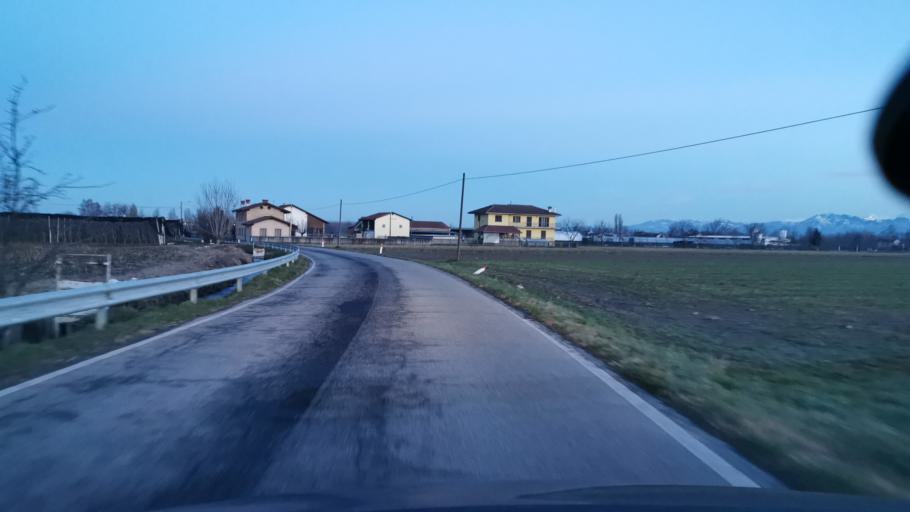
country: IT
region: Piedmont
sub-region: Provincia di Cuneo
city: Roata Rossi
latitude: 44.4575
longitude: 7.5148
